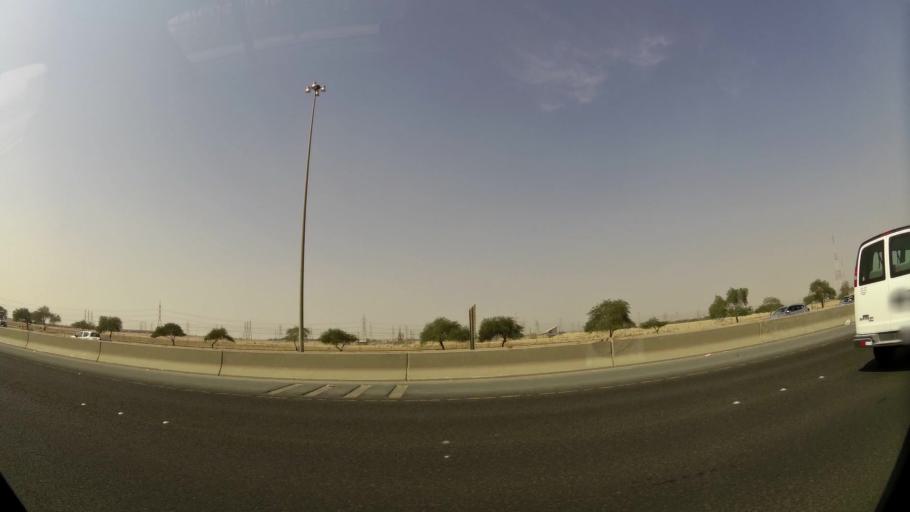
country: KW
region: Al Ahmadi
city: Al Fahahil
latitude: 29.0683
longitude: 48.1106
